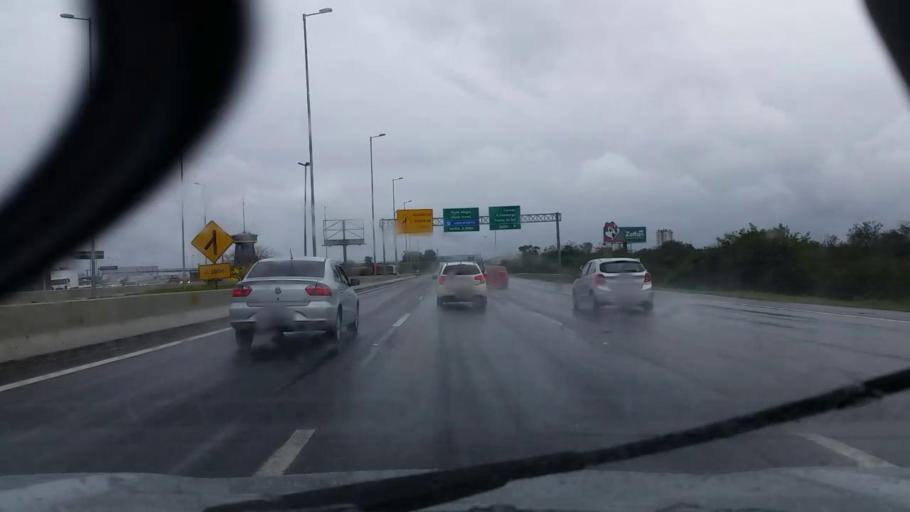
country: BR
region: Rio Grande do Sul
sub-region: Canoas
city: Canoas
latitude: -29.9689
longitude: -51.1677
